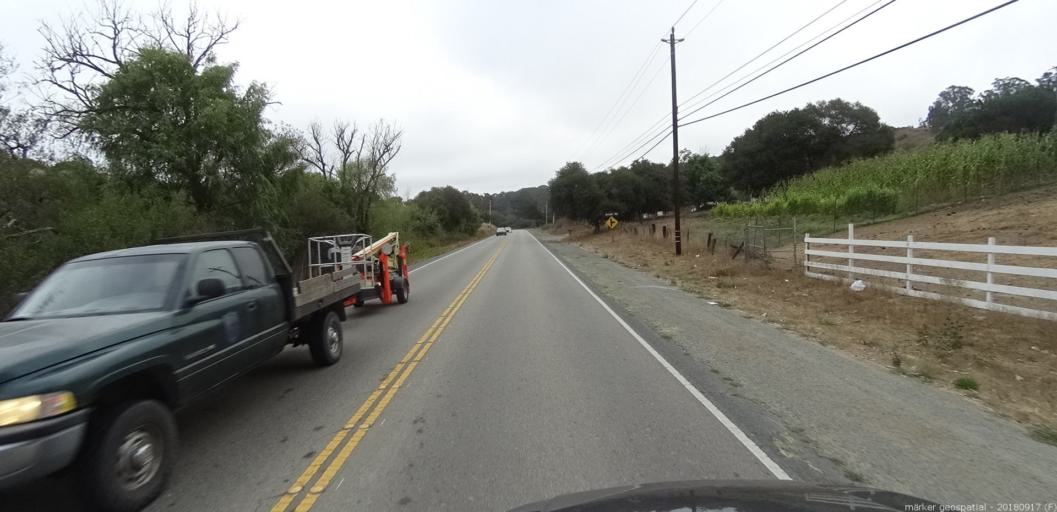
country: US
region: California
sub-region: Monterey County
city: Prunedale
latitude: 36.7952
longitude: -121.7059
